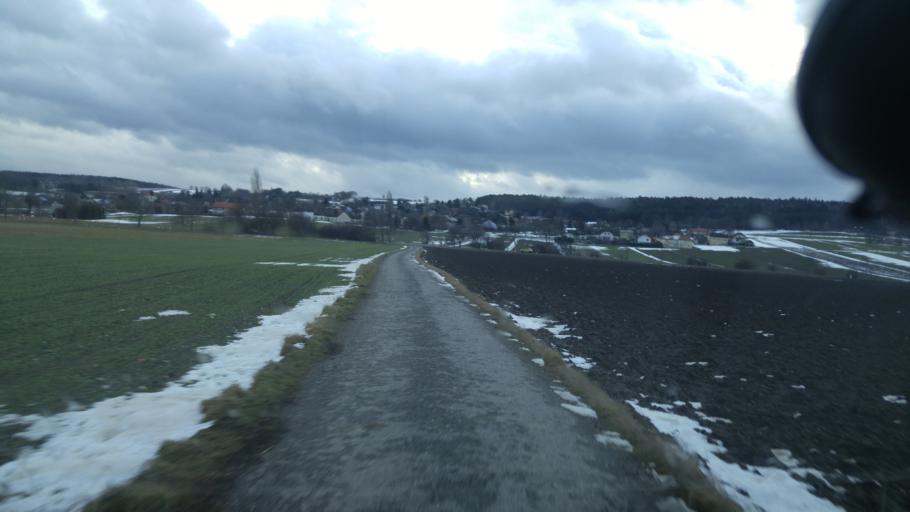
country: AT
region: Lower Austria
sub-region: Politischer Bezirk Baden
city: Hirtenberg
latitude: 47.9613
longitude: 16.1668
